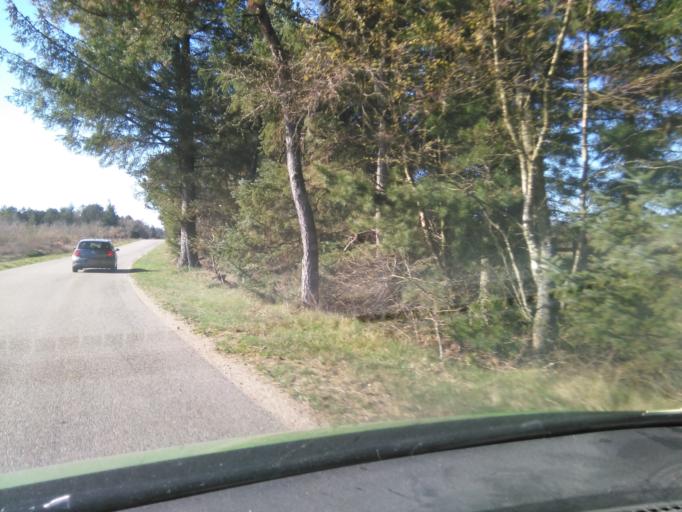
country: DK
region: South Denmark
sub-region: Varde Kommune
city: Oksbol
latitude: 55.6627
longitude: 8.2573
